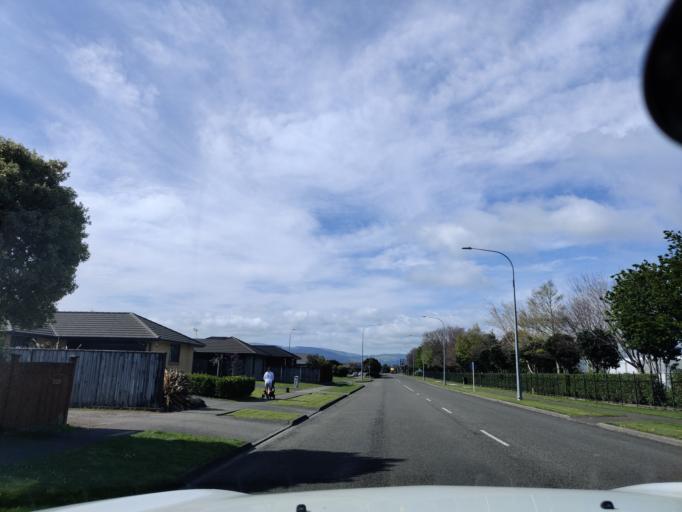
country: NZ
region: Manawatu-Wanganui
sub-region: Palmerston North City
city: Palmerston North
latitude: -40.3310
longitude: 175.6527
